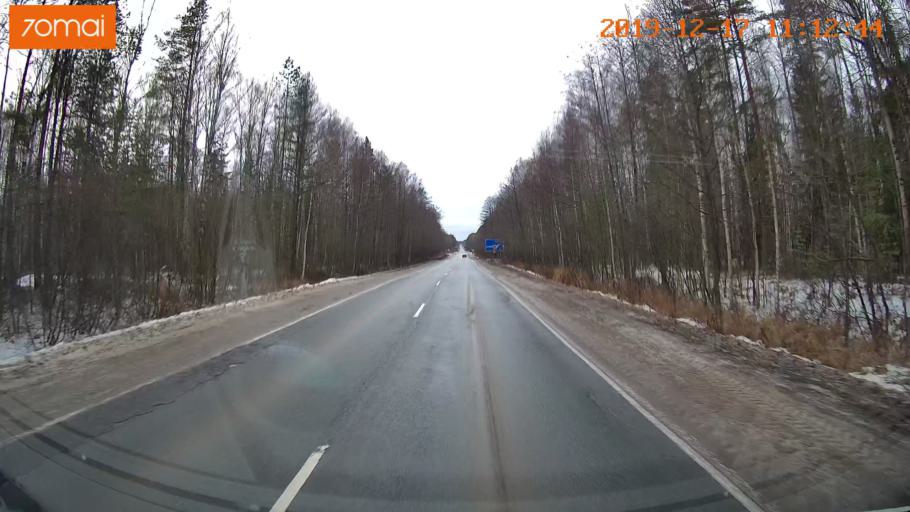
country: RU
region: Vladimir
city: Gus'-Khrustal'nyy
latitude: 55.5721
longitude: 40.6256
